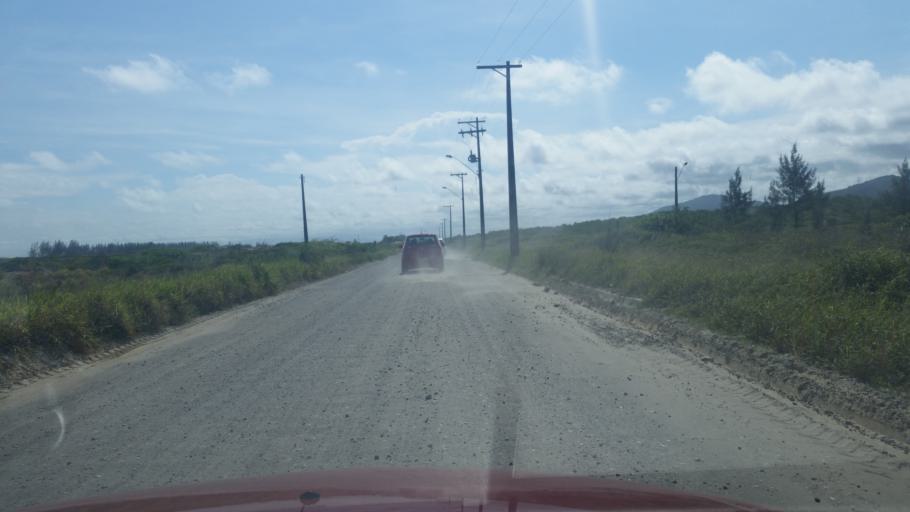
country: BR
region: Sao Paulo
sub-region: Iguape
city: Iguape
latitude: -24.7016
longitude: -47.4640
